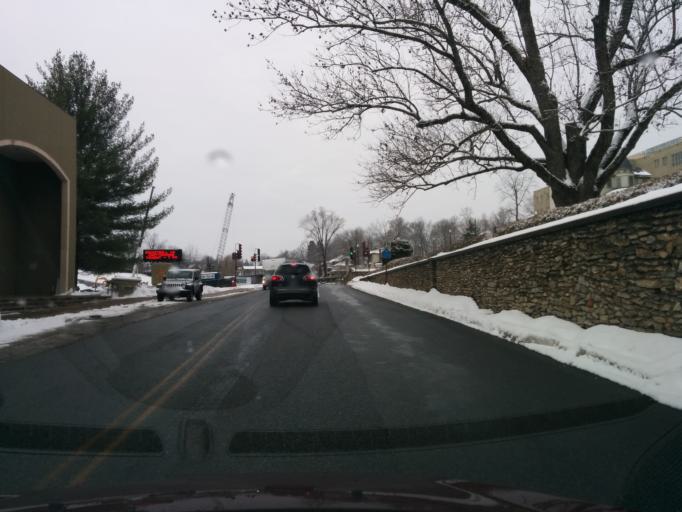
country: US
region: Virginia
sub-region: City of Lexington
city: Lexington
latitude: 37.7889
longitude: -79.4365
